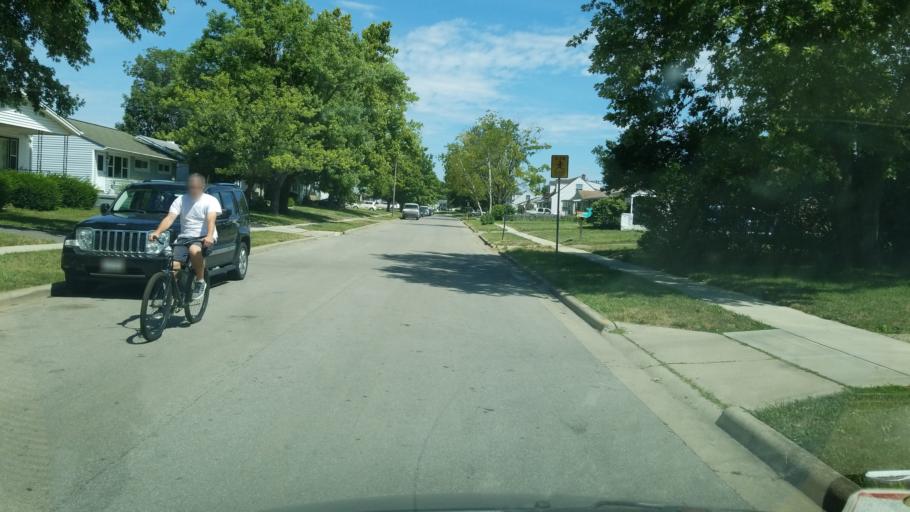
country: US
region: Ohio
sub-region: Franklin County
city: Grove City
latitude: 39.8773
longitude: -83.0777
